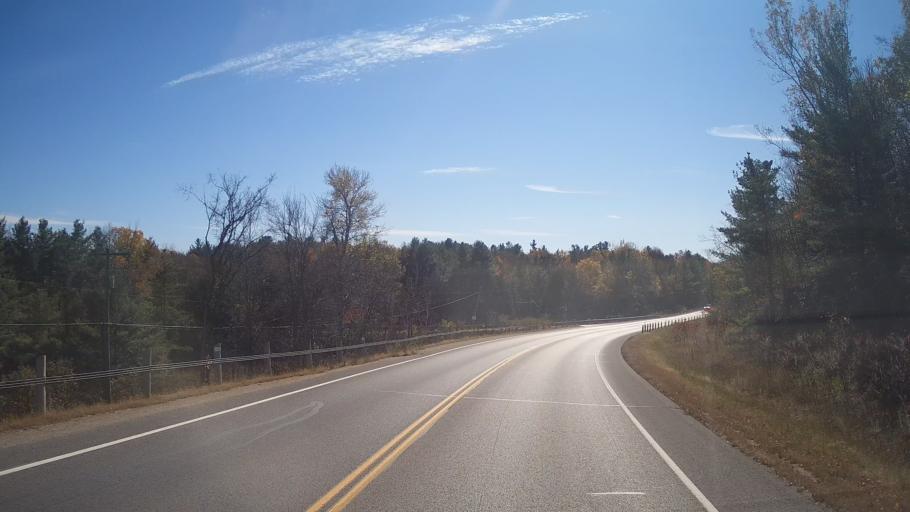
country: CA
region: Ontario
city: Perth
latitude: 44.7098
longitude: -76.6706
